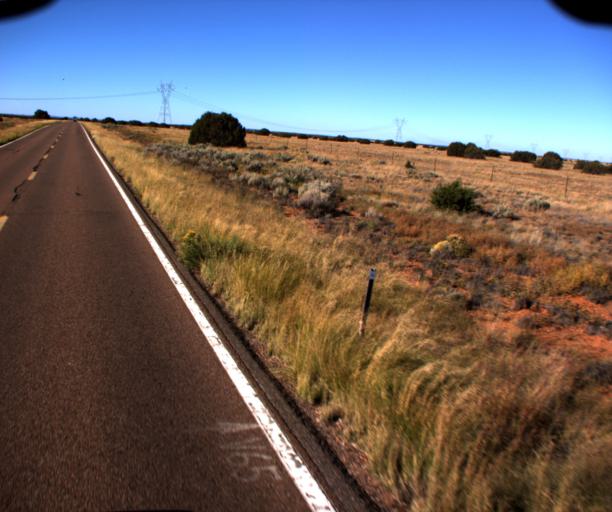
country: US
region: Arizona
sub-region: Navajo County
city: Heber-Overgaard
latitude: 34.5991
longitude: -110.3891
